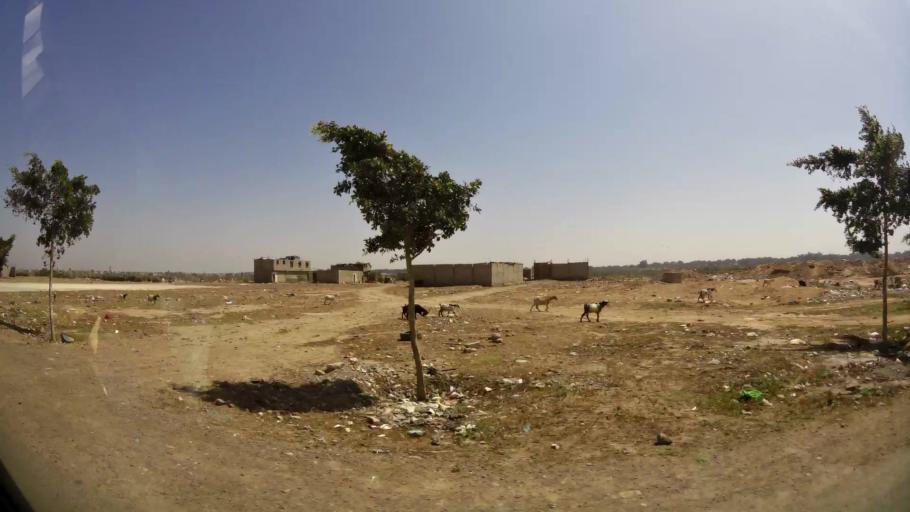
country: MA
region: Souss-Massa-Draa
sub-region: Inezgane-Ait Mellou
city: Inezgane
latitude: 30.3434
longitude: -9.5432
